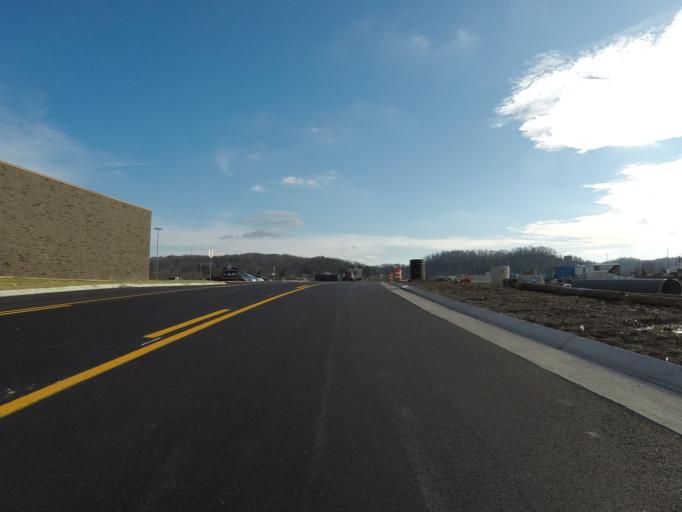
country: US
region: West Virginia
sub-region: Cabell County
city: Barboursville
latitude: 38.4141
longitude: -82.2897
